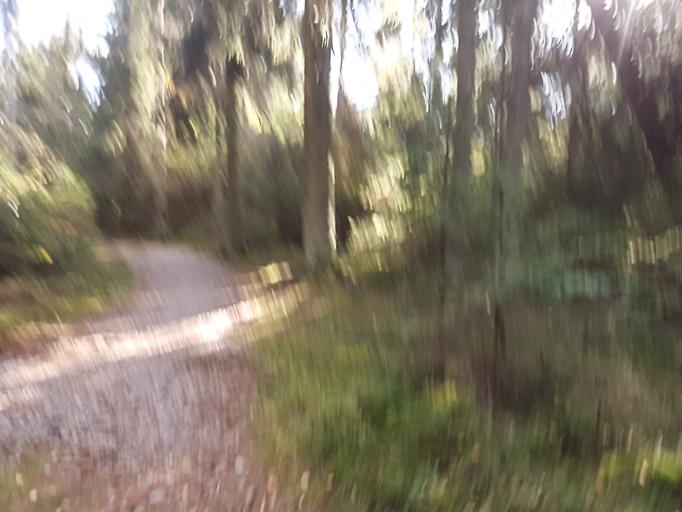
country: SE
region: Kronoberg
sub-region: Vaxjo Kommun
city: Vaexjoe
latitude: 56.8495
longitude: 14.8403
